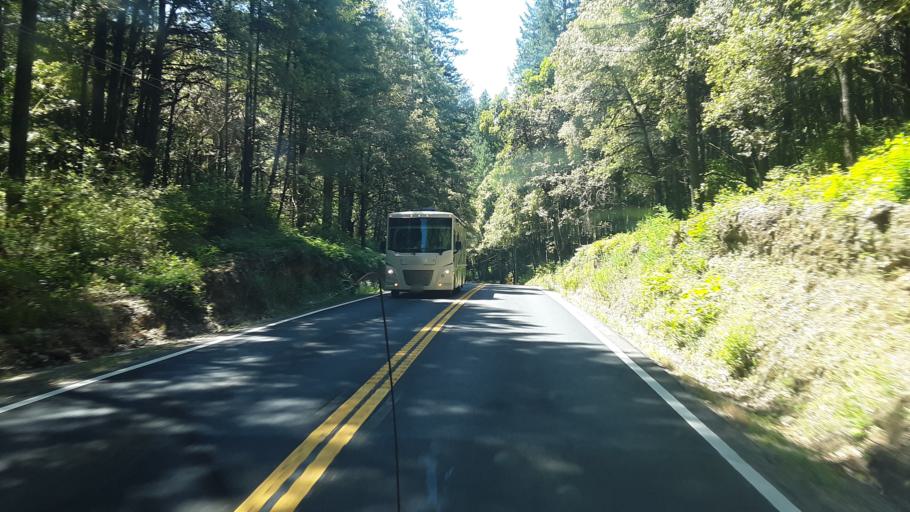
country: US
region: California
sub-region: Del Norte County
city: Bertsch-Oceanview
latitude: 41.8274
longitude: -124.0324
